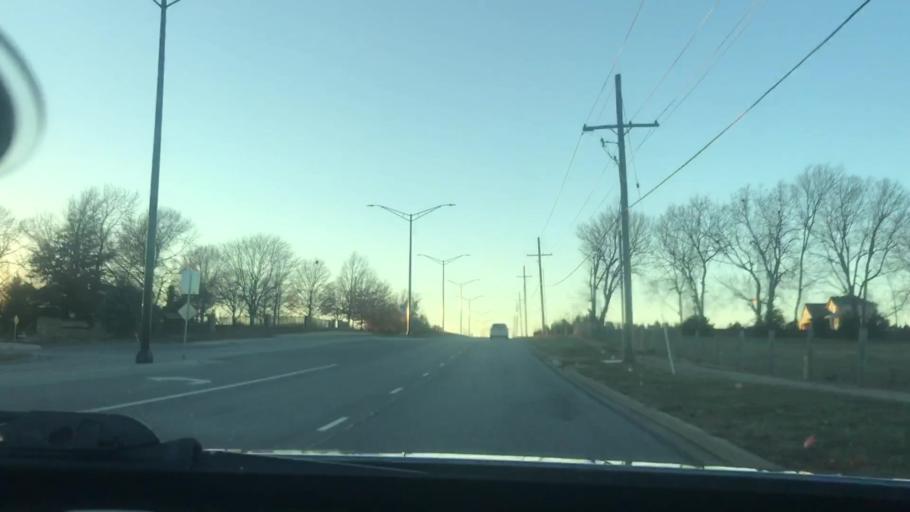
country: US
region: Kansas
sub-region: Johnson County
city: Olathe
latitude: 38.9274
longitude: -94.8212
